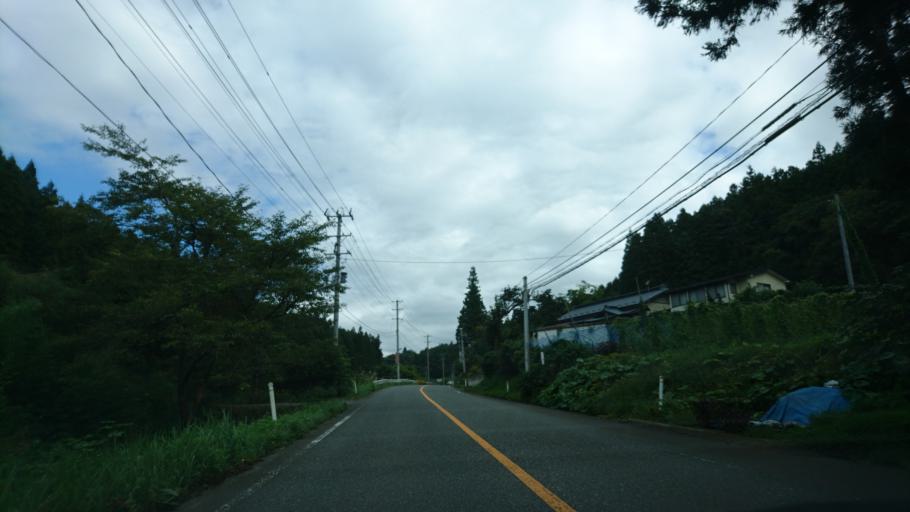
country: JP
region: Miyagi
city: Furukawa
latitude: 38.7688
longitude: 140.8630
